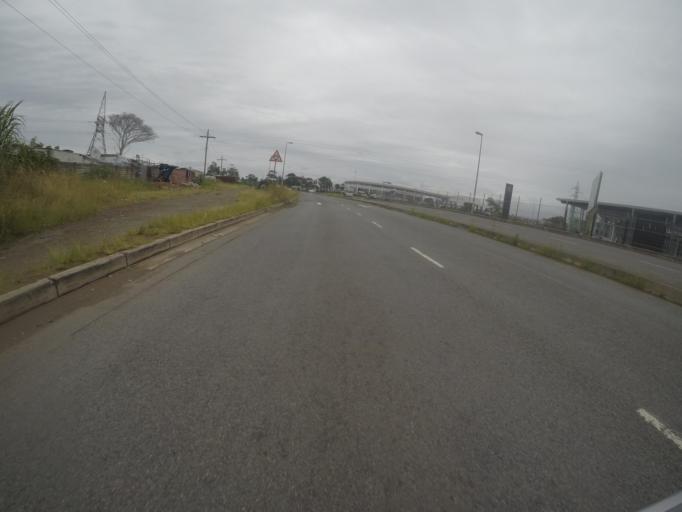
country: ZA
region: Eastern Cape
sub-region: Buffalo City Metropolitan Municipality
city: East London
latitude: -32.9492
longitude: 27.9238
